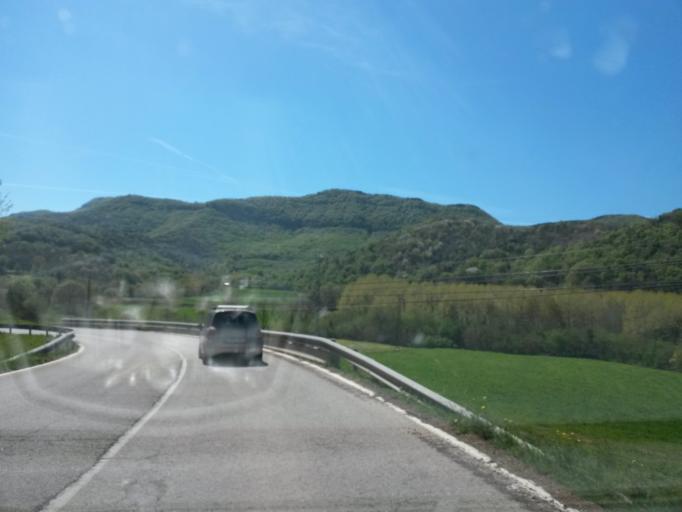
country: ES
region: Catalonia
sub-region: Provincia de Girona
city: Santa Pau
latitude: 42.1458
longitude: 2.5602
